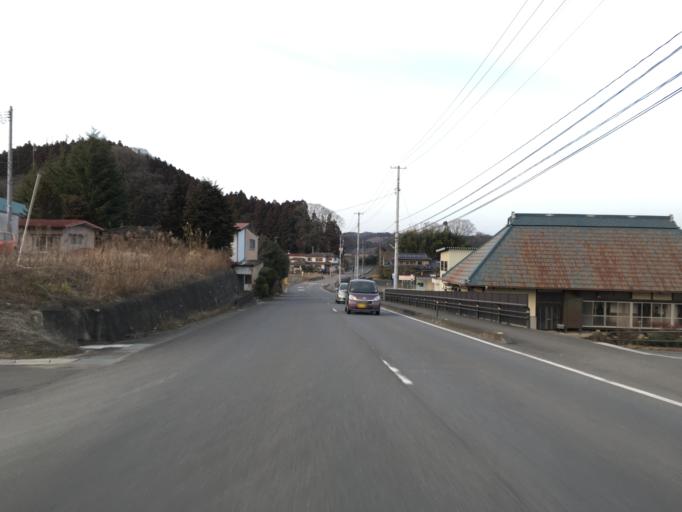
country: JP
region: Ibaraki
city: Daigo
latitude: 36.9552
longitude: 140.4048
